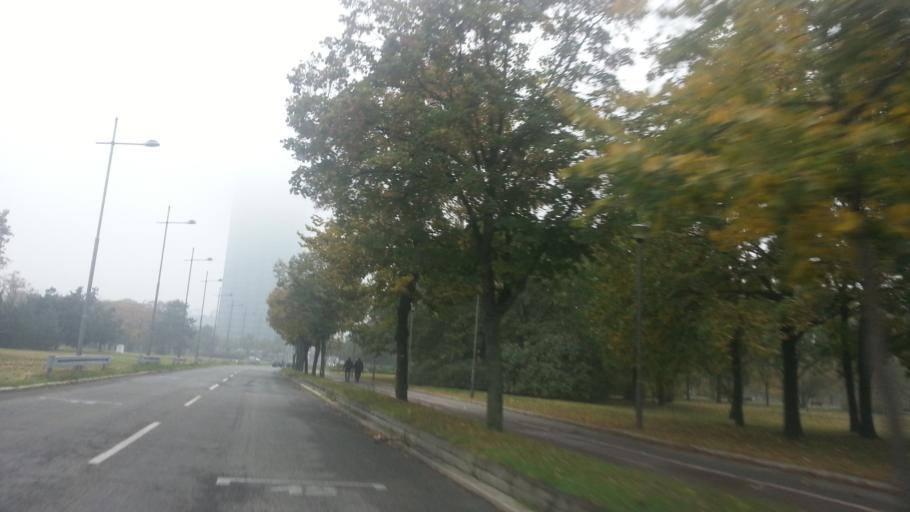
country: RS
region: Central Serbia
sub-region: Belgrade
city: Novi Beograd
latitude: 44.8202
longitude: 20.4390
